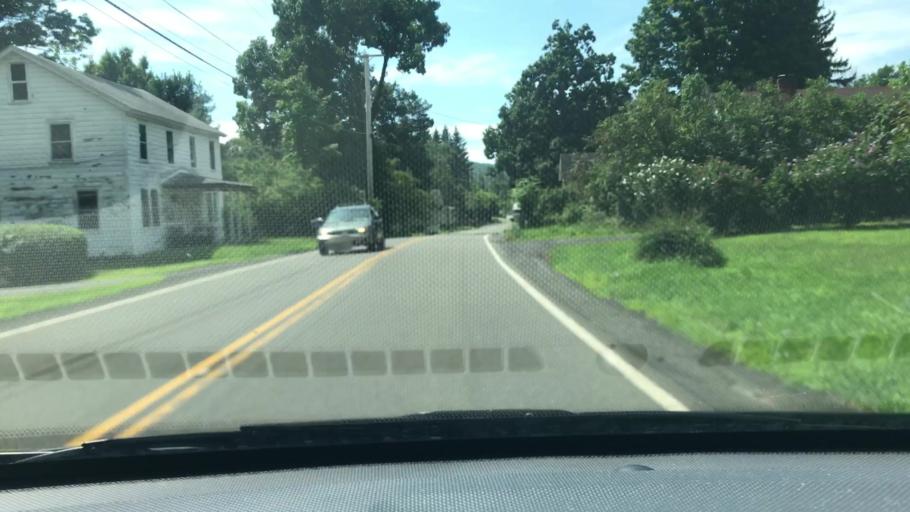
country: US
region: New York
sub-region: Ulster County
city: Shokan
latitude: 41.9294
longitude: -74.2159
